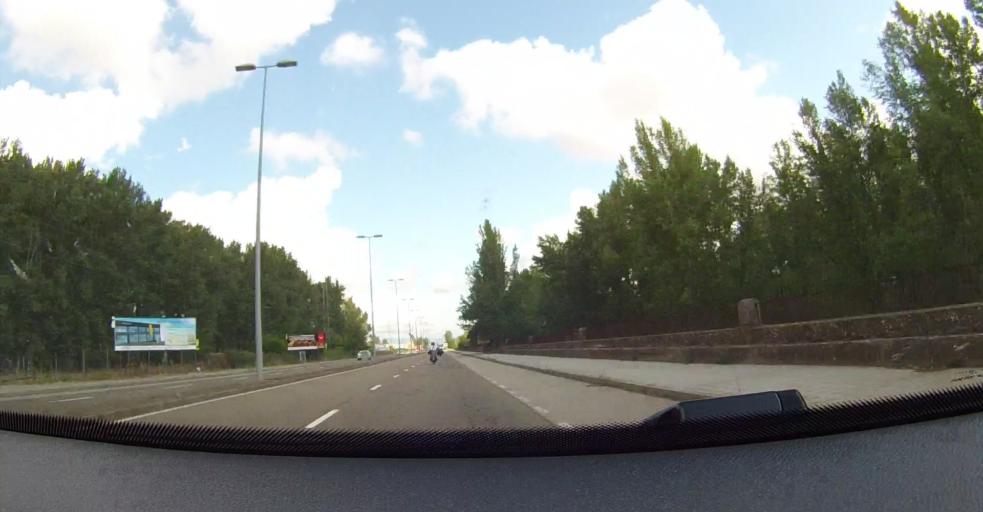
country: ES
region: Castille and Leon
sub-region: Provincia de Leon
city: Leon
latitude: 42.5757
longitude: -5.5693
